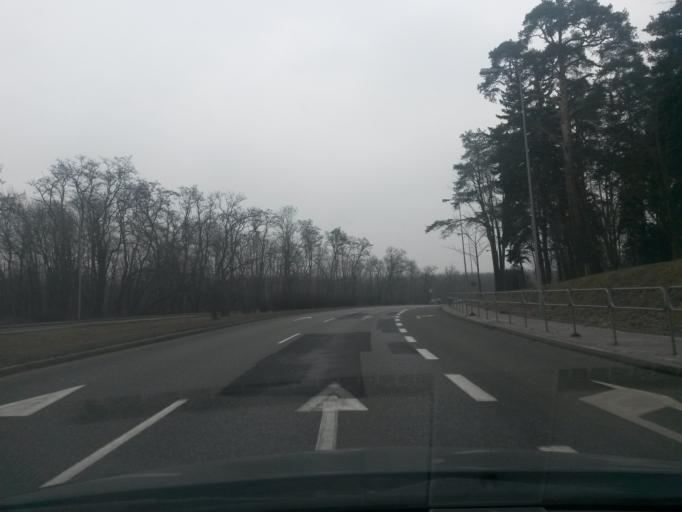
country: PL
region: Masovian Voivodeship
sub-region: Powiat legionowski
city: Nieporet
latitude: 52.4644
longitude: 21.0223
